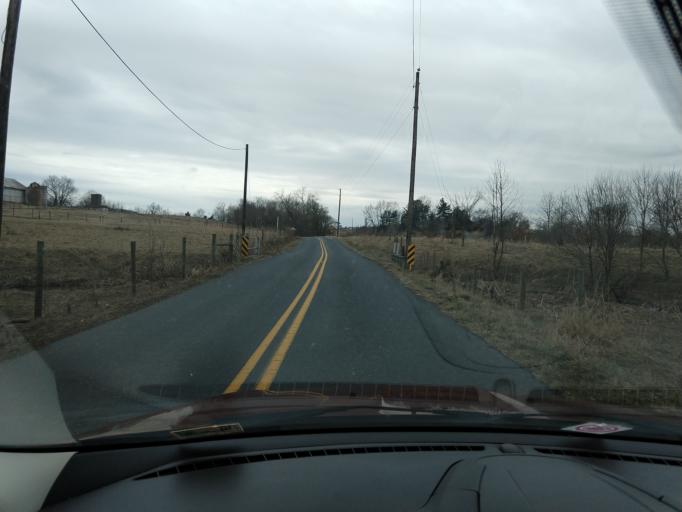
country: US
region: Virginia
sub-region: Augusta County
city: Weyers Cave
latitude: 38.2248
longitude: -78.8887
